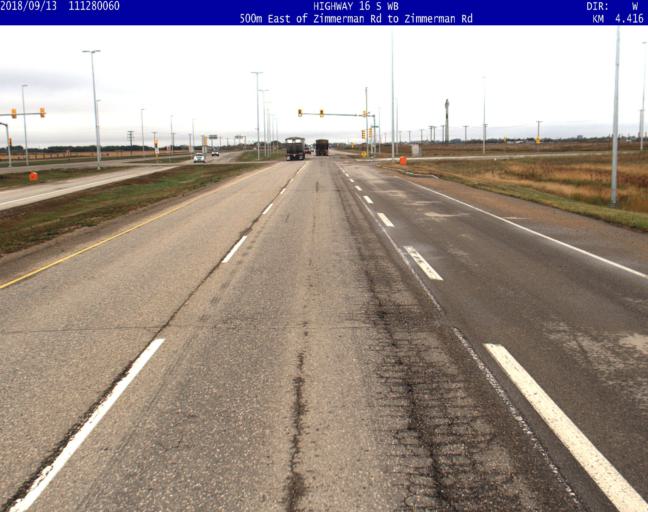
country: CA
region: Saskatchewan
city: Saskatoon
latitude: 52.0862
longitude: -106.5341
